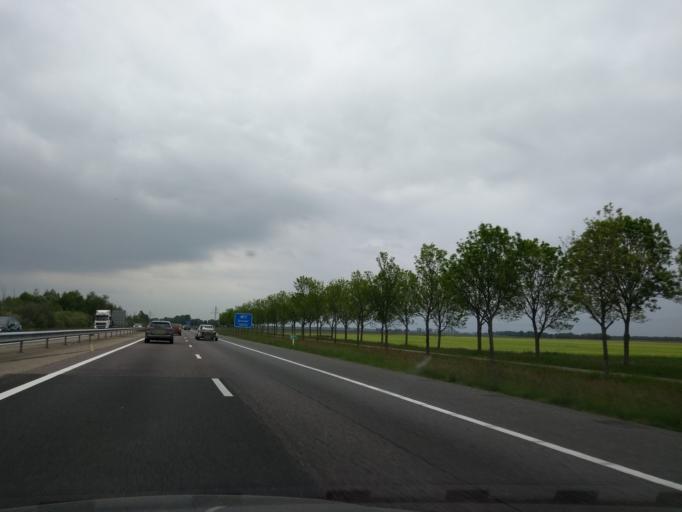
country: NL
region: Drenthe
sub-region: Gemeente Meppel
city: Meppel
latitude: 52.7110
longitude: 6.2055
